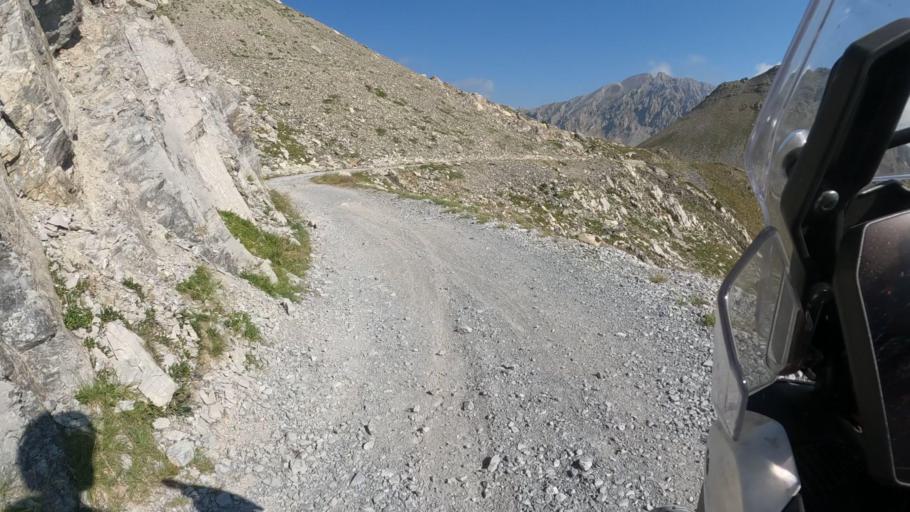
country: IT
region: Piedmont
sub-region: Provincia di Cuneo
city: Pietraporzio
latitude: 44.3940
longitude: 7.0237
